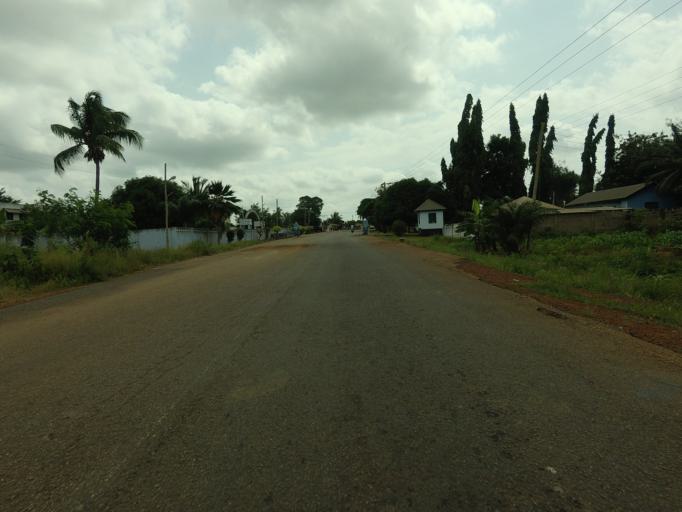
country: TG
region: Maritime
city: Lome
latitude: 6.1736
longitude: 1.0733
